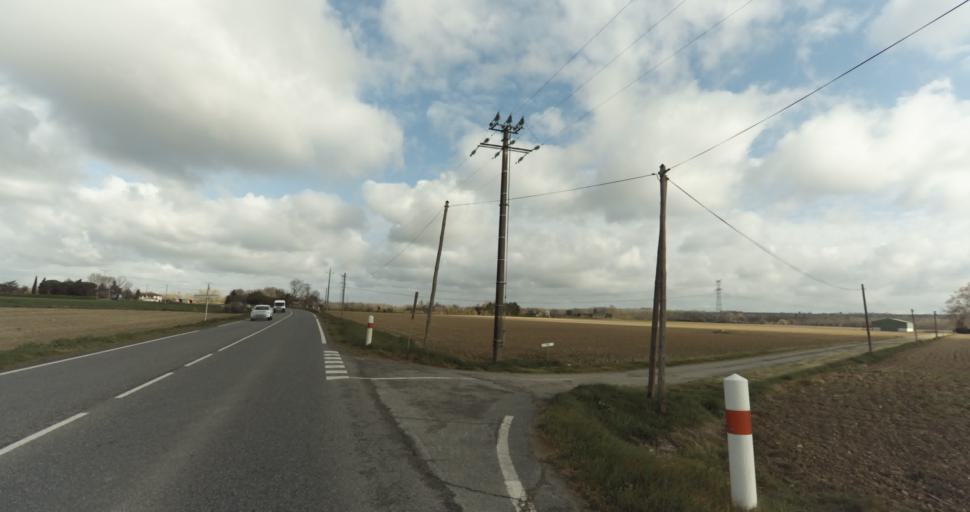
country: FR
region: Midi-Pyrenees
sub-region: Departement de la Haute-Garonne
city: Miremont
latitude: 43.3807
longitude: 1.4445
